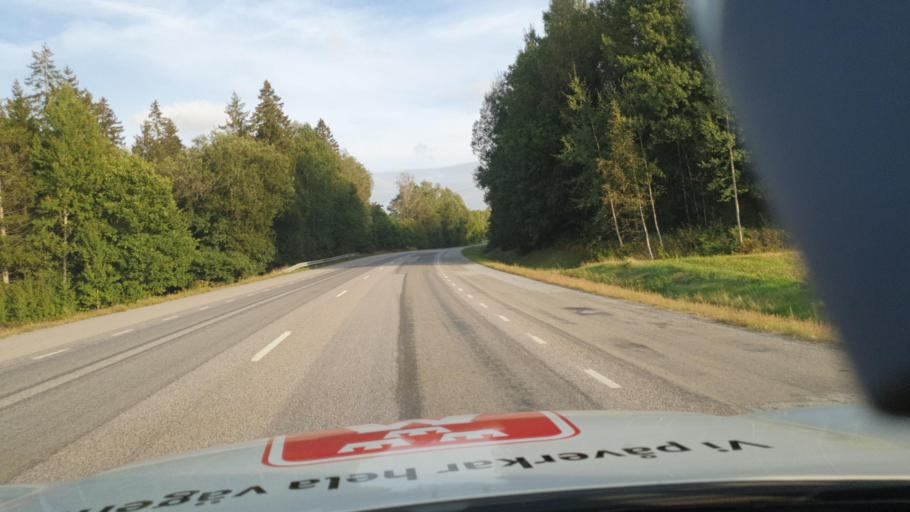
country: SE
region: Vaestra Goetaland
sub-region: Uddevalla Kommun
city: Ljungskile
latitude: 58.1946
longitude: 11.9324
